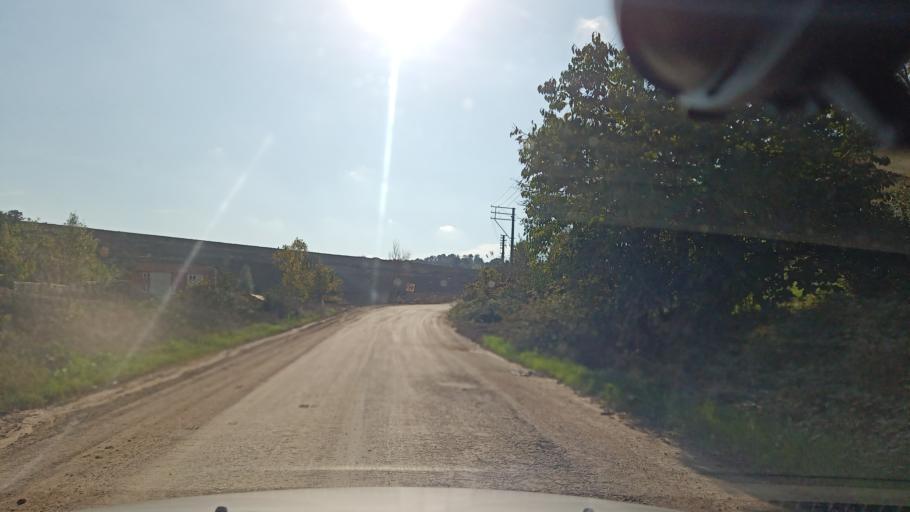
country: TR
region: Sakarya
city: Ferizli
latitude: 41.1046
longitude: 30.4761
